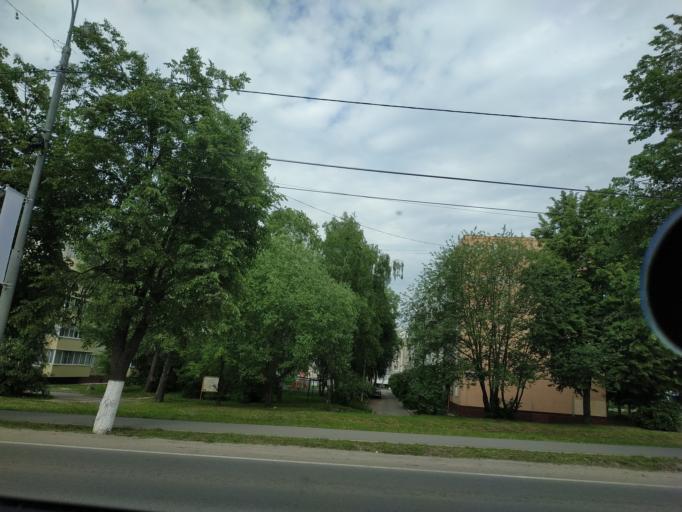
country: RU
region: Moskovskaya
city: Bronnitsy
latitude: 55.4197
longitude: 38.2778
